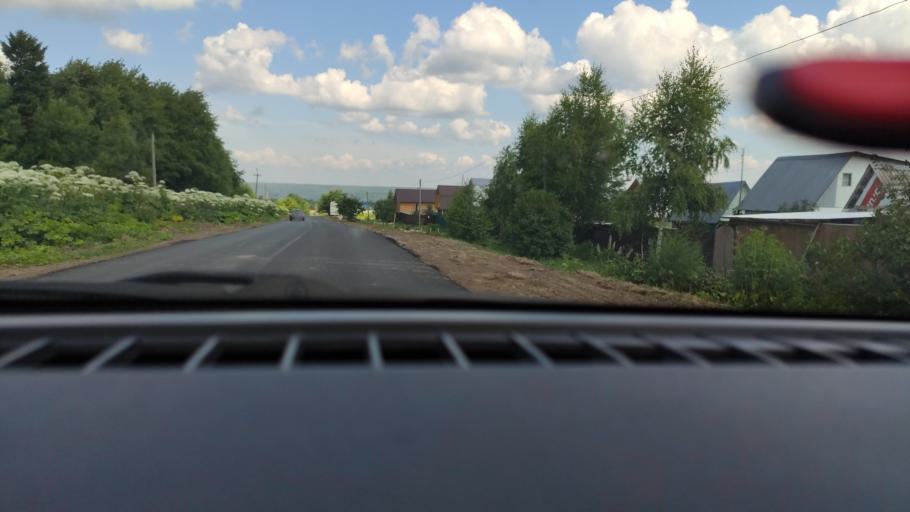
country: RU
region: Perm
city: Sylva
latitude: 58.0330
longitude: 56.7225
